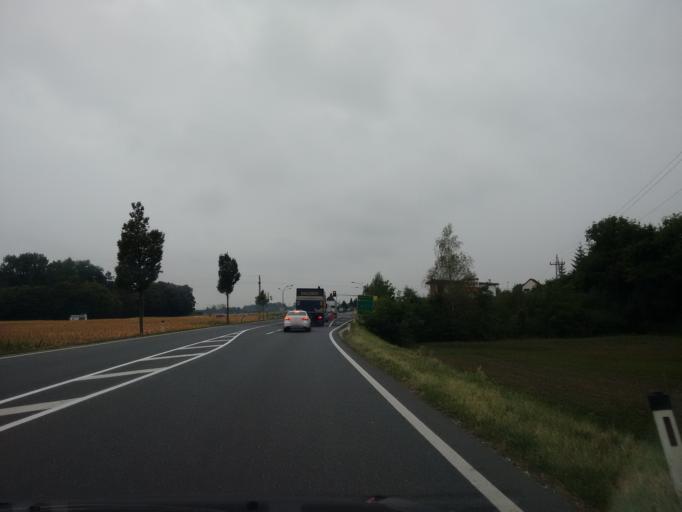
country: AT
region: Upper Austria
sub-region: Wels-Land
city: Marchtrenk
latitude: 48.1889
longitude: 14.1132
